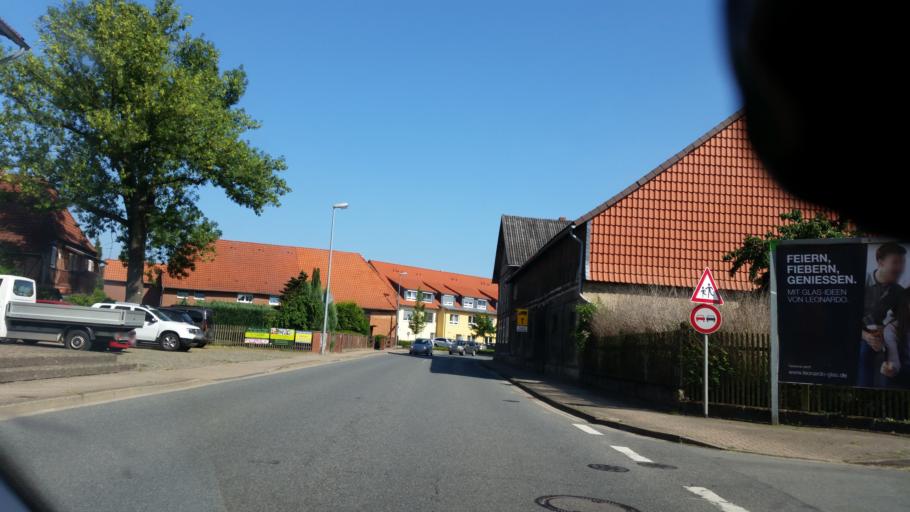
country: DE
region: Lower Saxony
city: Wolfsburg
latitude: 52.3503
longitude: 10.7772
